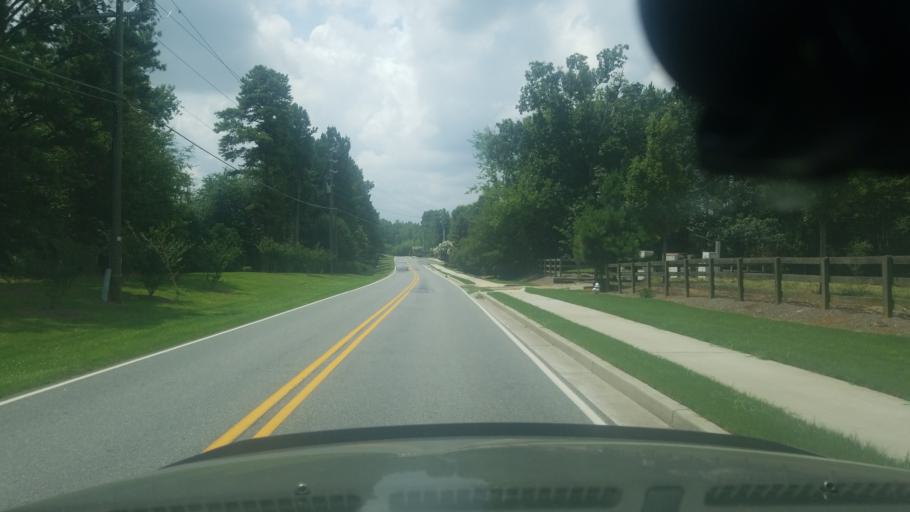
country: US
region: Georgia
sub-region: Fulton County
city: Johns Creek
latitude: 34.1081
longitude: -84.1894
